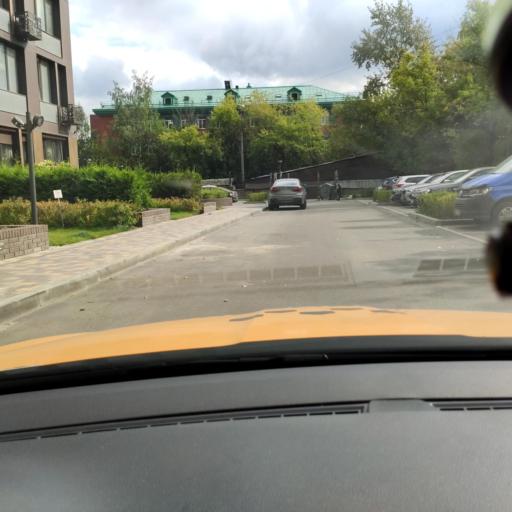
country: RU
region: Moscow
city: Sokol'niki
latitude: 55.8114
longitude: 37.6487
